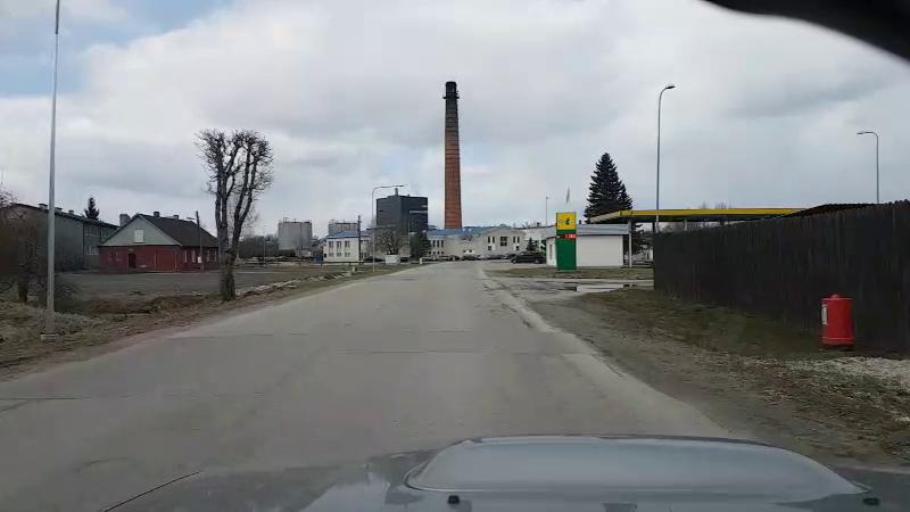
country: EE
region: Jaervamaa
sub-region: Paide linn
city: Paide
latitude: 58.8813
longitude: 25.5540
